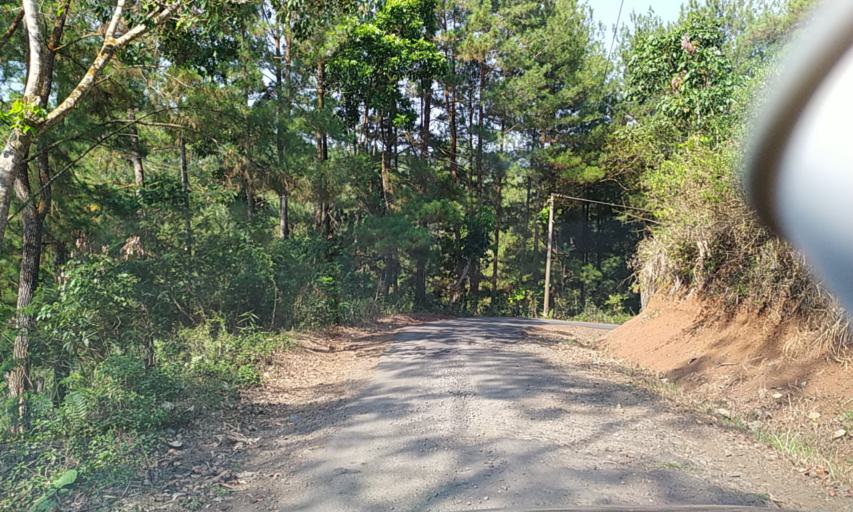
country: ID
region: Central Java
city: Datar
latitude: -7.2148
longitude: 108.6272
